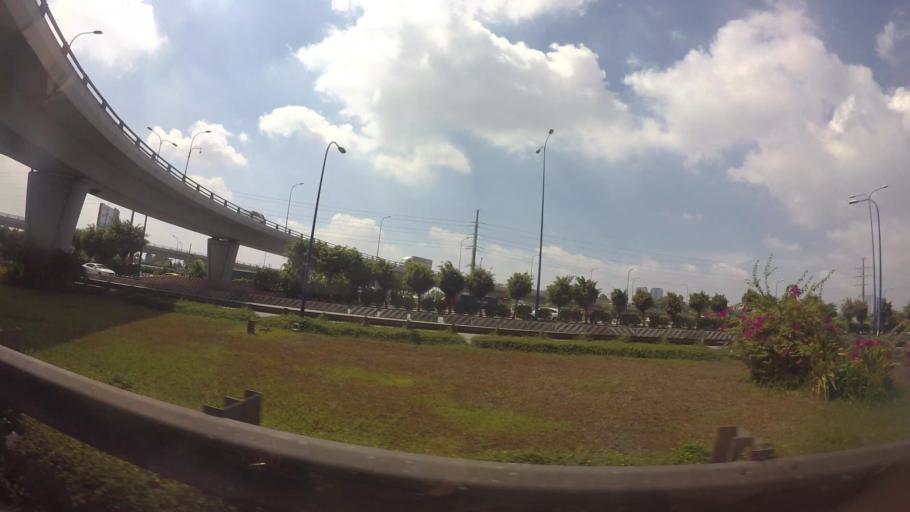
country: VN
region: Ho Chi Minh City
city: Quan Hai
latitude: 10.8045
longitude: 106.7531
